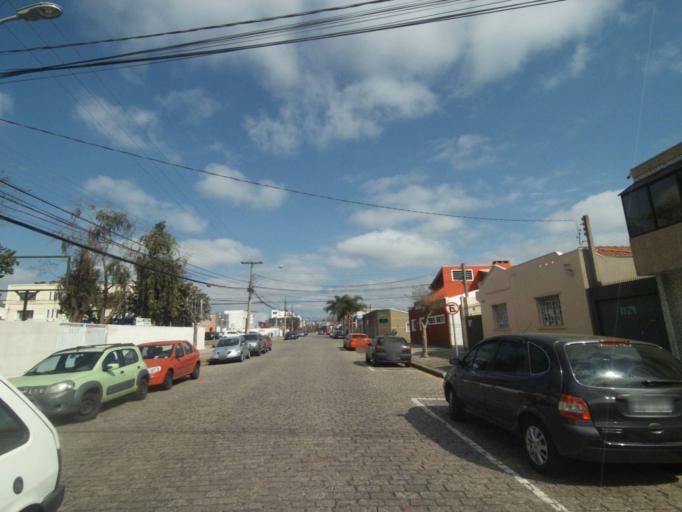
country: BR
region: Parana
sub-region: Curitiba
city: Curitiba
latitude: -25.4462
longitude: -49.2626
